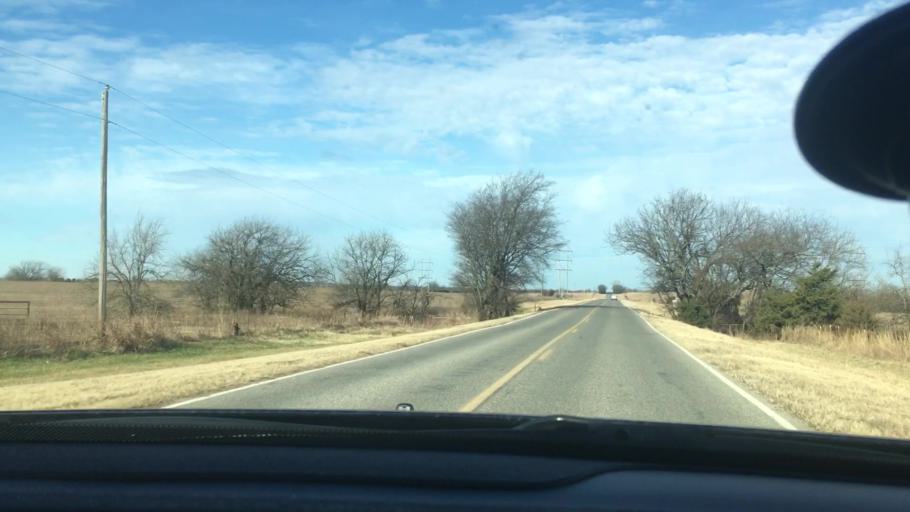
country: US
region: Oklahoma
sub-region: Seminole County
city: Konawa
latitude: 34.9723
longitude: -96.7798
